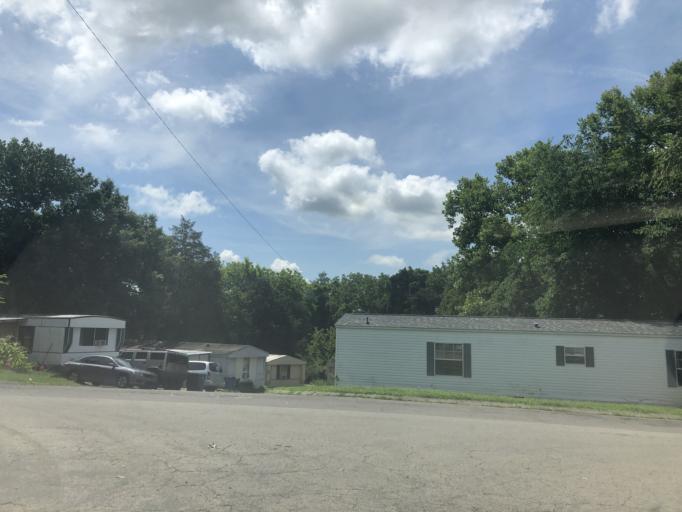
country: US
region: Tennessee
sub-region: Davidson County
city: Lakewood
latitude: 36.2595
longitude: -86.6779
